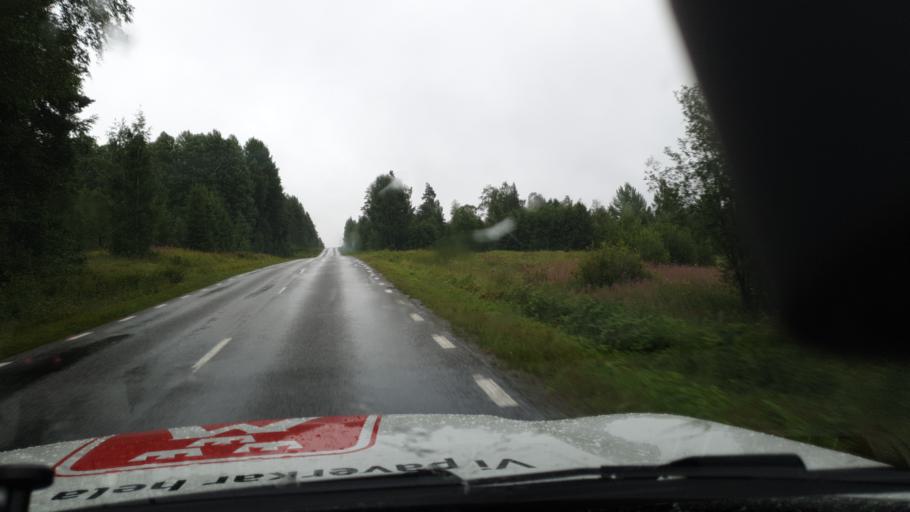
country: SE
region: Vaesterbotten
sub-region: Skelleftea Kommun
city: Viken
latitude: 64.6684
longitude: 20.8541
